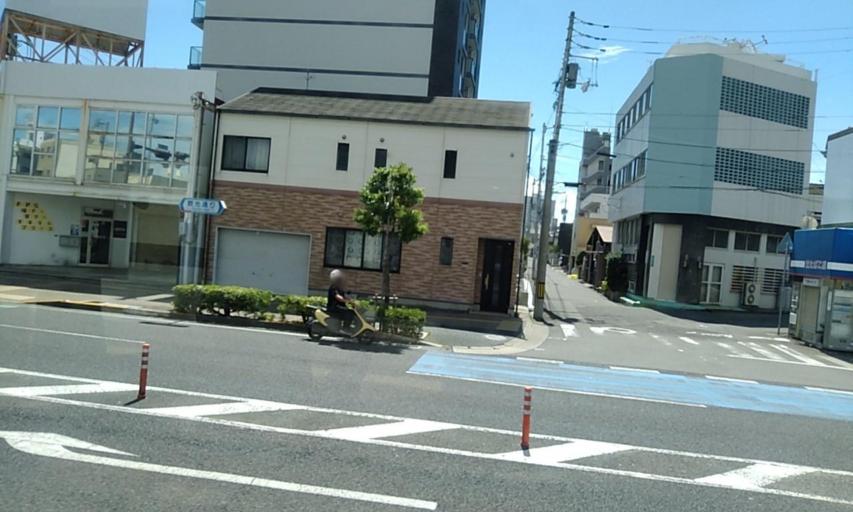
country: JP
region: Kagawa
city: Takamatsu-shi
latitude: 34.3362
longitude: 134.0536
